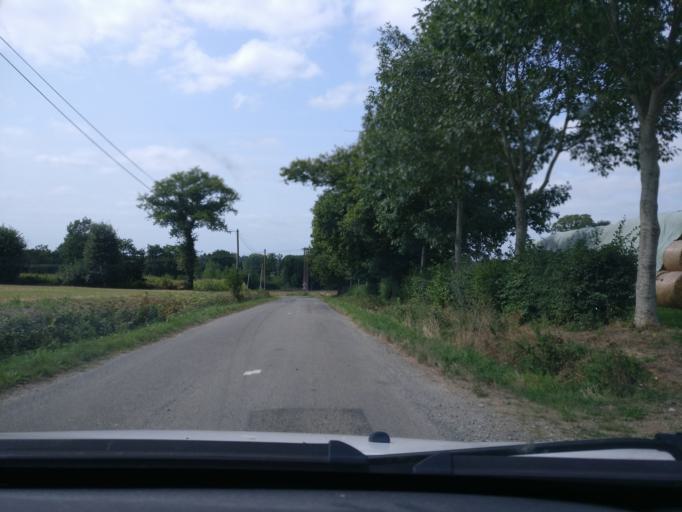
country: FR
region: Brittany
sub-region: Departement d'Ille-et-Vilaine
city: Betton
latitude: 48.1538
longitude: -1.6369
